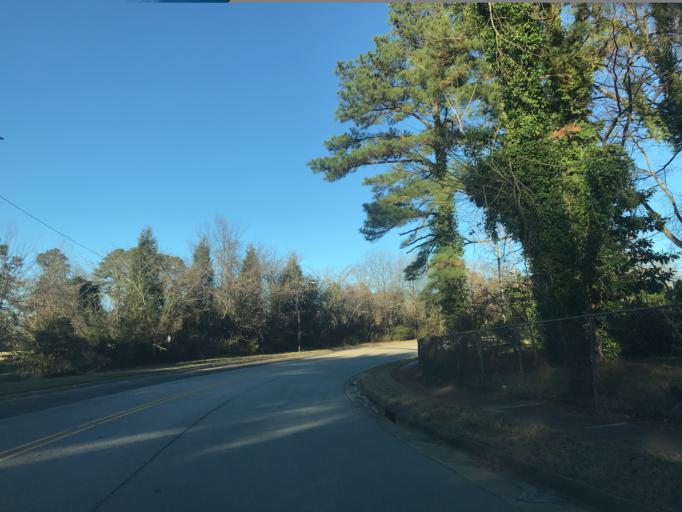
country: US
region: North Carolina
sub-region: Wake County
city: Raleigh
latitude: 35.7862
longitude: -78.6231
